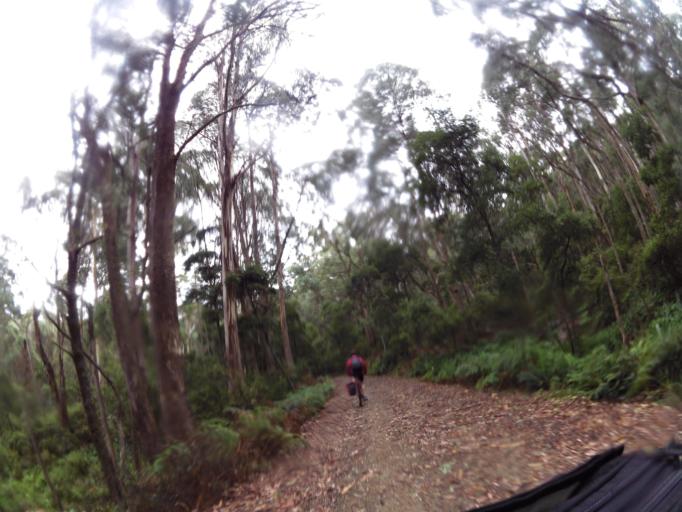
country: AU
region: New South Wales
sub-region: Greater Hume Shire
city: Holbrook
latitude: -36.1969
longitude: 147.5220
